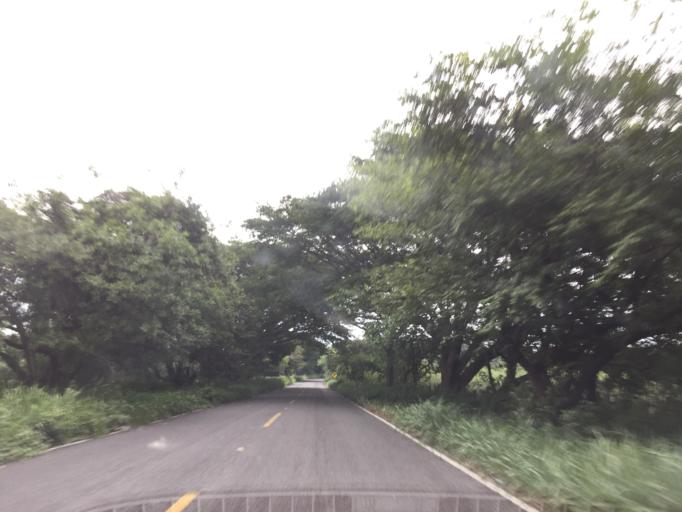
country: MX
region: Colima
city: Comala
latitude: 19.3482
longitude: -103.7874
